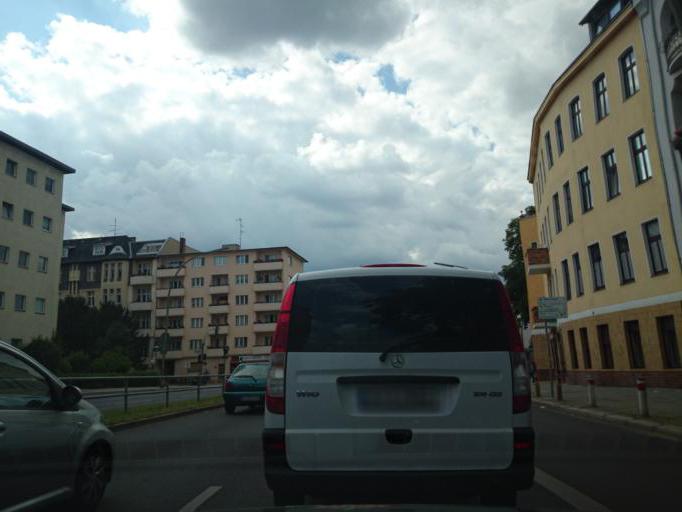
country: DE
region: Berlin
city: Steglitz Bezirk
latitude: 52.4513
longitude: 13.3361
